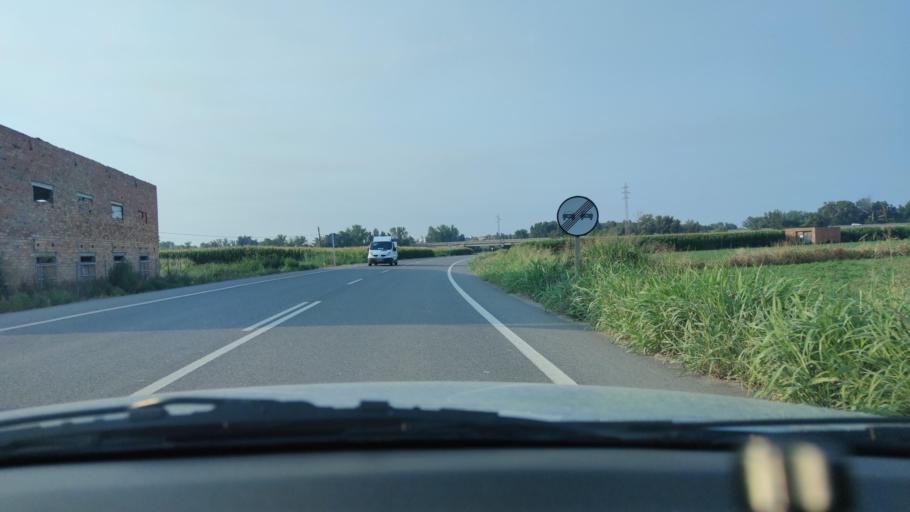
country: ES
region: Catalonia
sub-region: Provincia de Lleida
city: Torres de Segre
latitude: 41.5439
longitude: 0.5129
